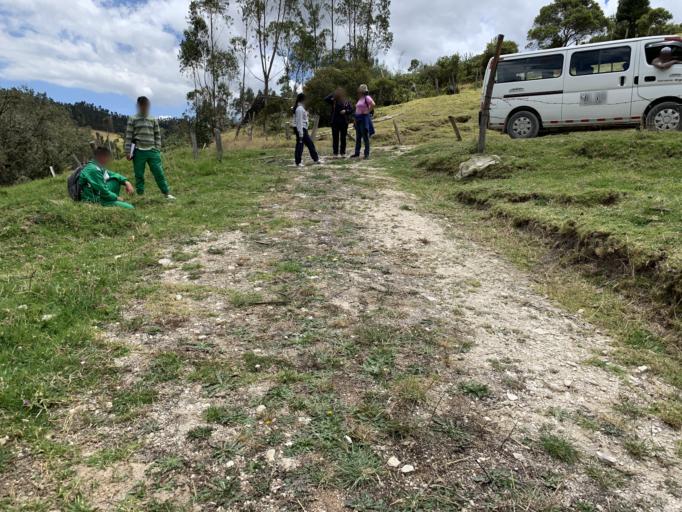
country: CO
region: Boyaca
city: Tuta
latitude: 5.7017
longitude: -73.1625
